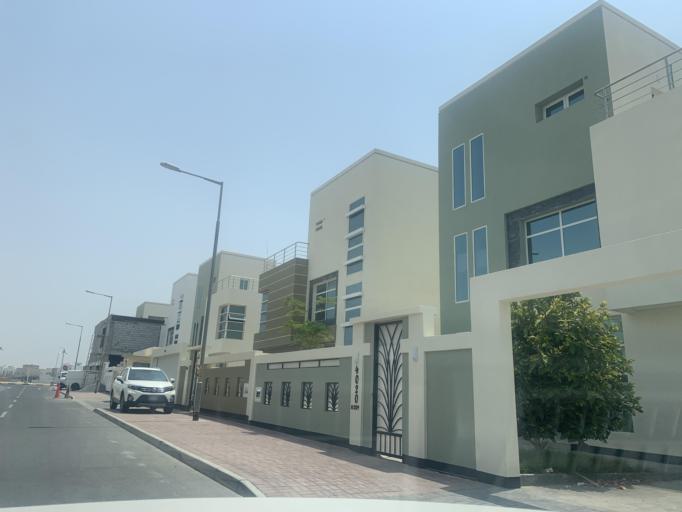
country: BH
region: Central Governorate
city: Madinat Hamad
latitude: 26.1345
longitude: 50.4678
